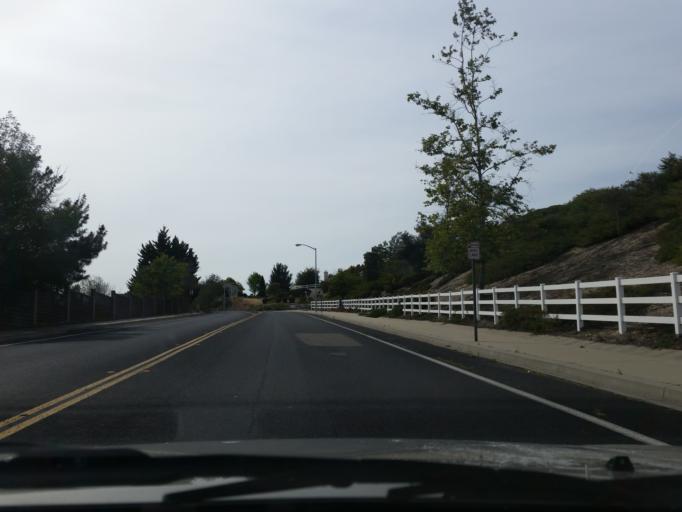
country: US
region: California
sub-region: San Luis Obispo County
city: Arroyo Grande
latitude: 35.1333
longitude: -120.5799
